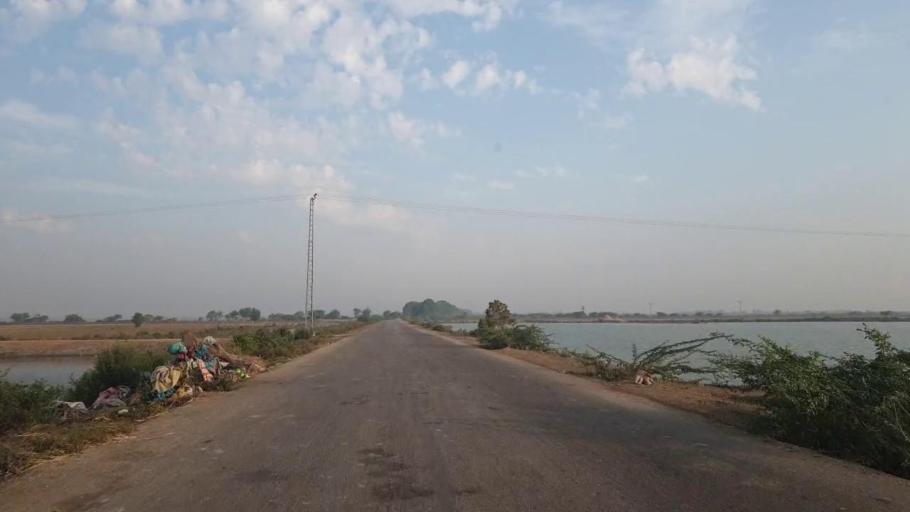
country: PK
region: Sindh
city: Tando Bago
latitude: 24.7226
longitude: 68.9422
